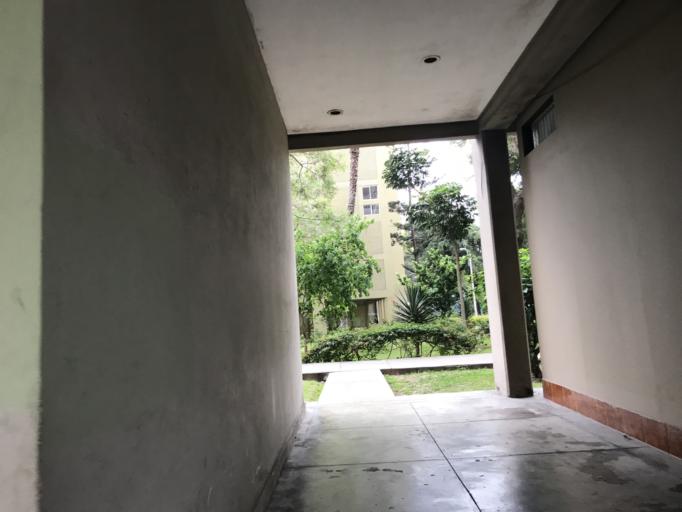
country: PE
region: Lima
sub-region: Lima
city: San Isidro
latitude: -12.0863
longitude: -77.0512
